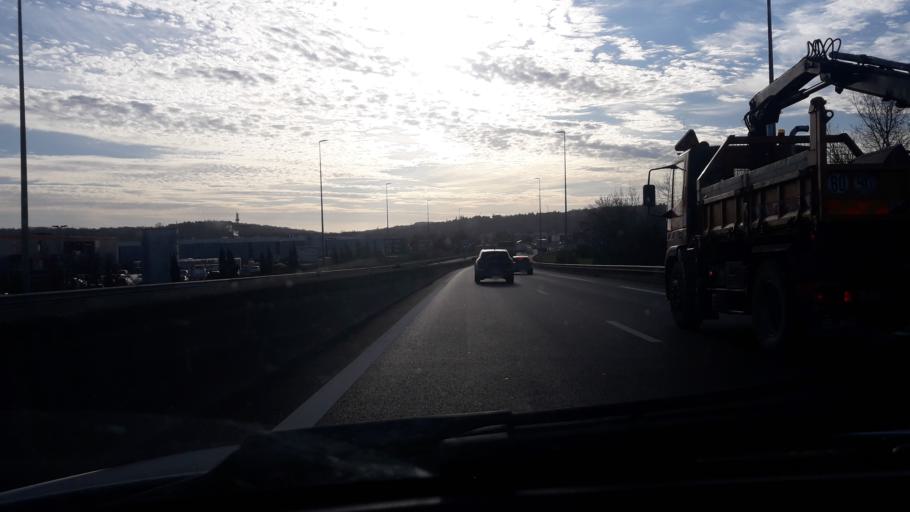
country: FR
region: Midi-Pyrenees
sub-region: Departement de la Haute-Garonne
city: Portet-sur-Garonne
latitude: 43.5531
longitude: 1.4125
